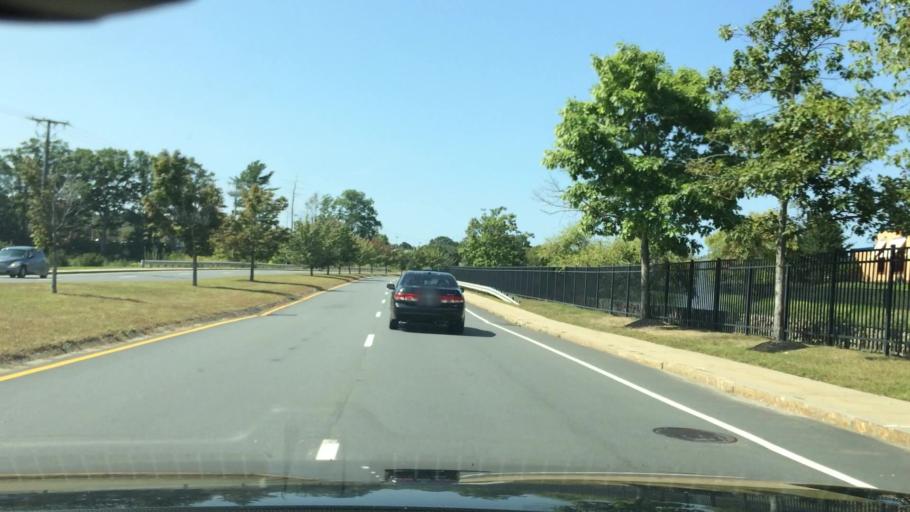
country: US
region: Massachusetts
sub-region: Essex County
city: Lawrence
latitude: 42.7420
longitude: -71.1571
